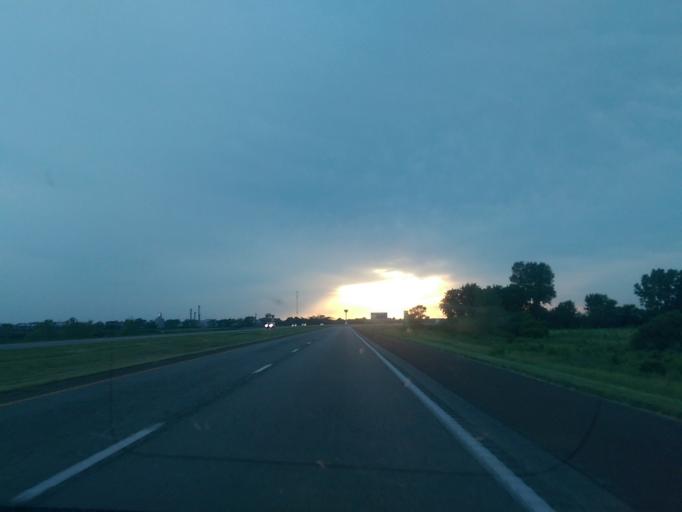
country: US
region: Missouri
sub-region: Holt County
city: Mound City
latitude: 40.1884
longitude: -95.3497
